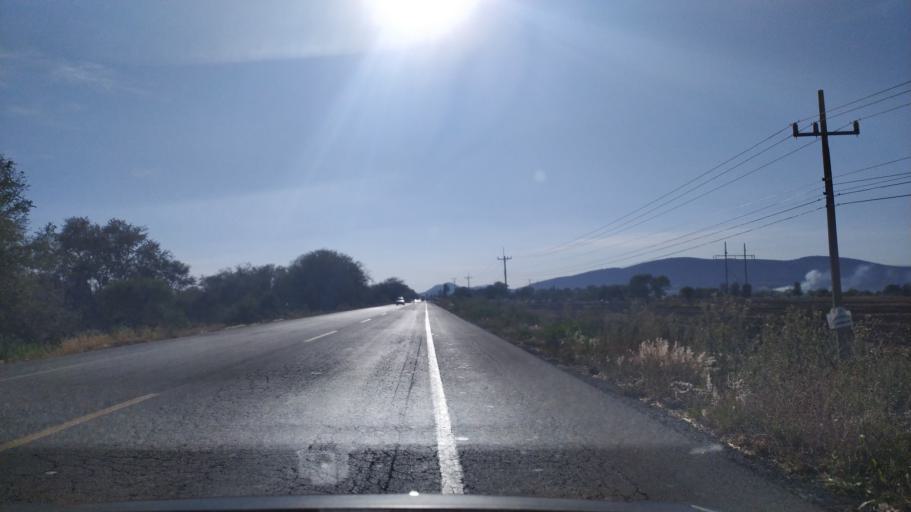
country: MX
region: Michoacan
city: Brisenas
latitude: 20.2932
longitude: -102.6255
